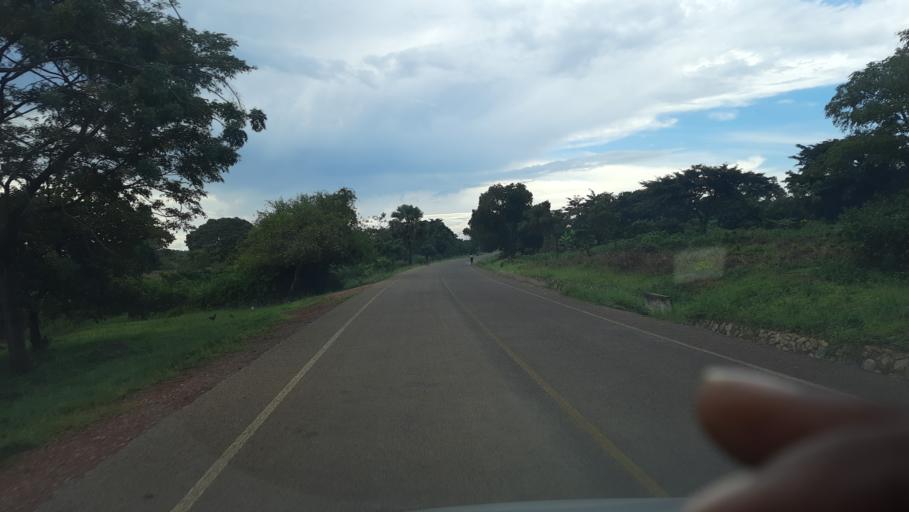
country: UG
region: Central Region
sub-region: Nakasongola District
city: Nakasongola
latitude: 1.3157
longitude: 32.4390
